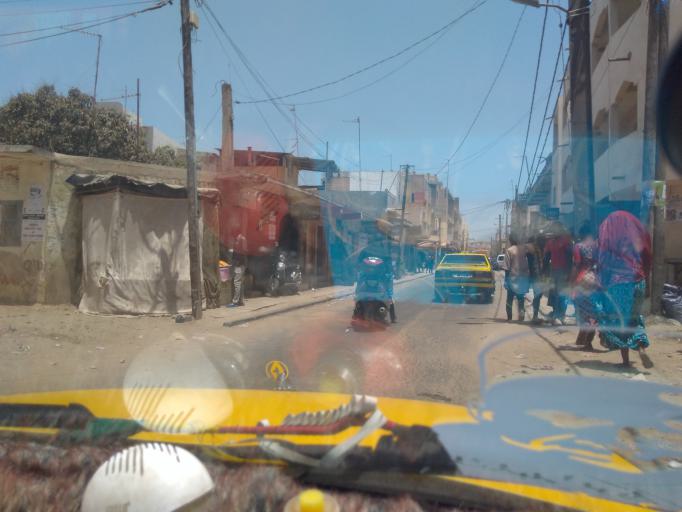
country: SN
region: Dakar
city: Grand Dakar
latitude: 14.7406
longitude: -17.4476
